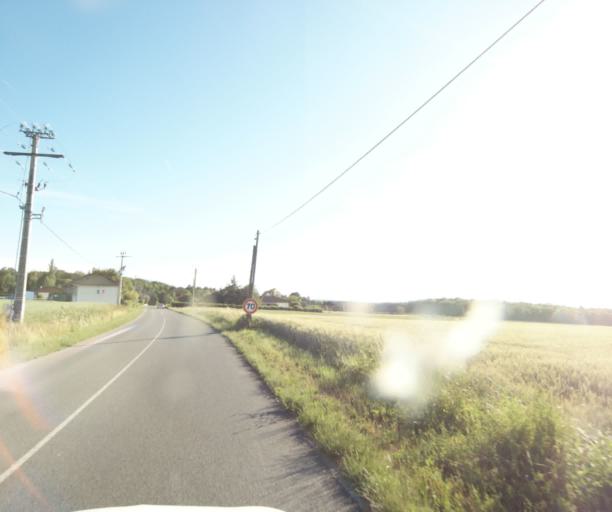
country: FR
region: Rhone-Alpes
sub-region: Departement de la Haute-Savoie
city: Loisin
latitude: 46.2698
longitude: 6.3097
